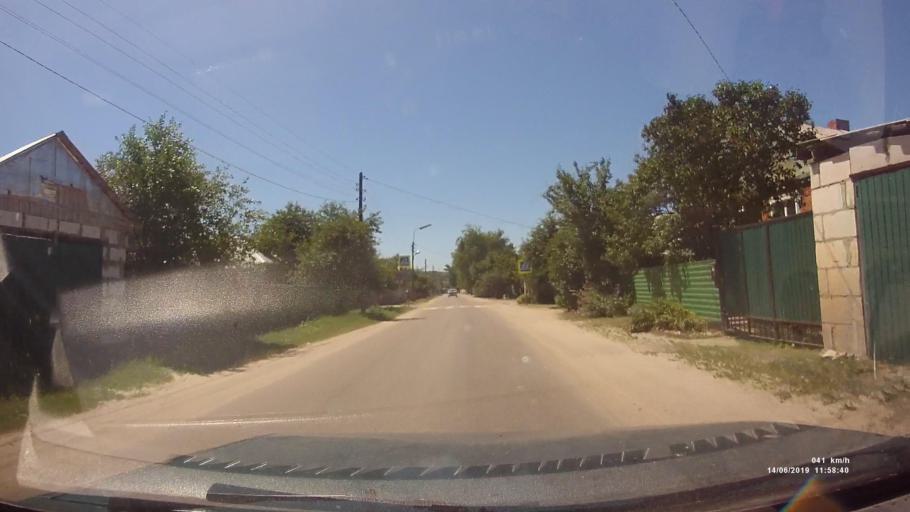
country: RU
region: Rostov
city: Kazanskaya
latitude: 49.7952
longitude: 41.1405
